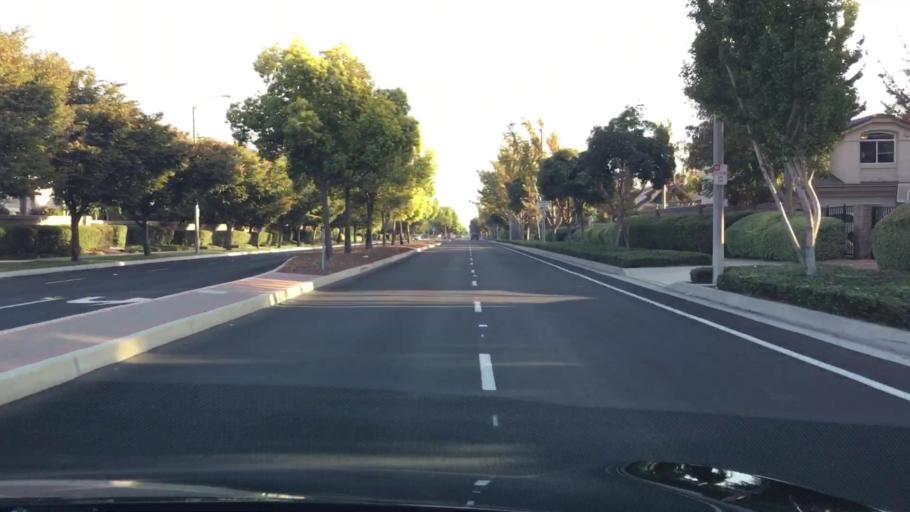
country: US
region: California
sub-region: San Bernardino County
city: Chino
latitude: 34.0117
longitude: -117.6545
